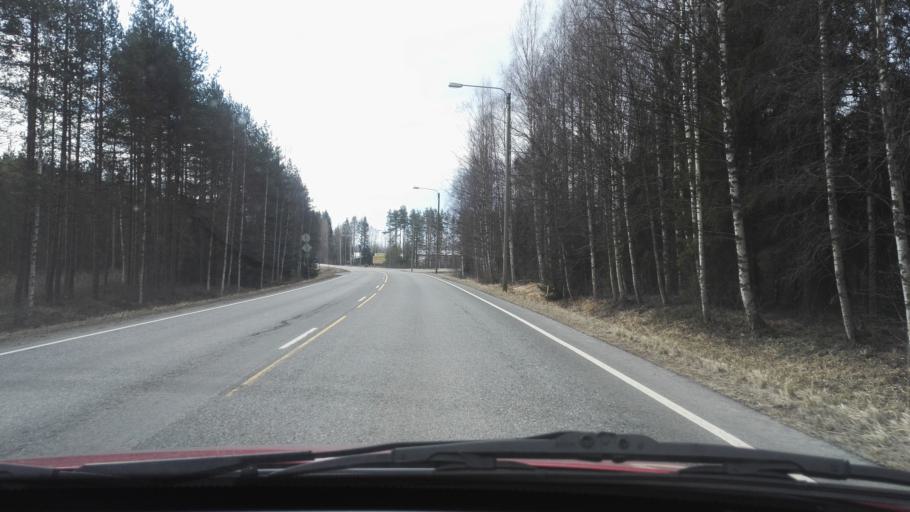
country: FI
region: Central Finland
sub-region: Jyvaeskylae
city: Petaejaevesi
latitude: 62.2689
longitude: 25.1707
